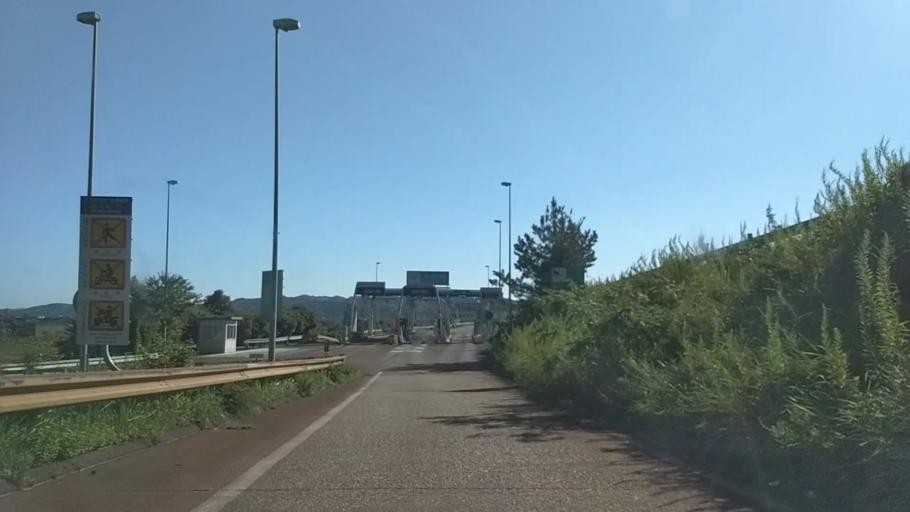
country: JP
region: Ishikawa
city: Kanazawa-shi
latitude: 36.6076
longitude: 136.6752
